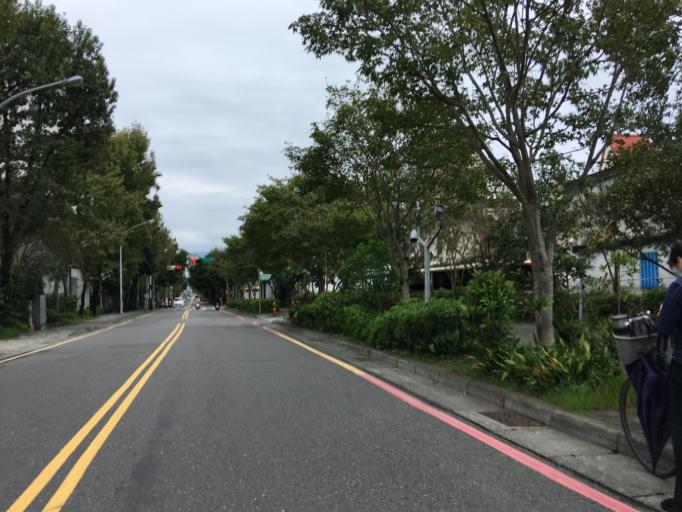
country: TW
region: Taiwan
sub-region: Yilan
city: Yilan
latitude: 24.7472
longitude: 121.7482
